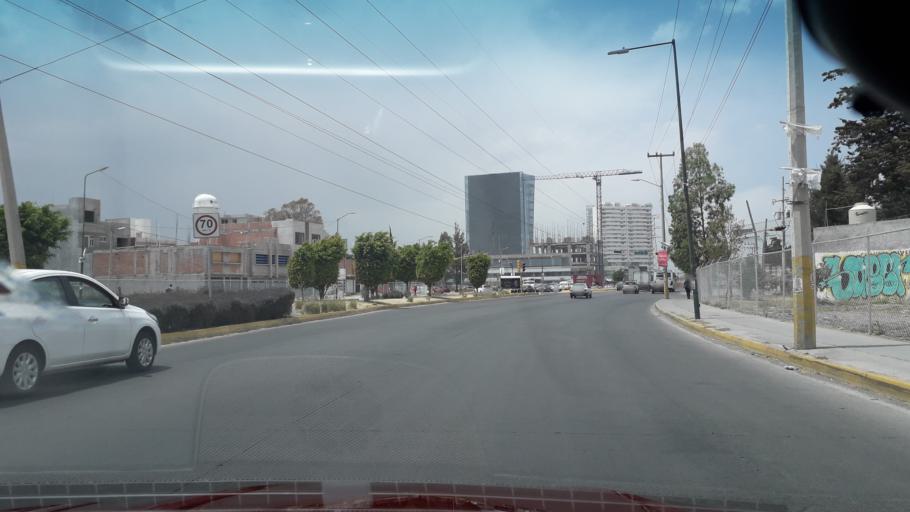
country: MX
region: Puebla
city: Tlazcalancingo
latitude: 19.0069
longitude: -98.2435
